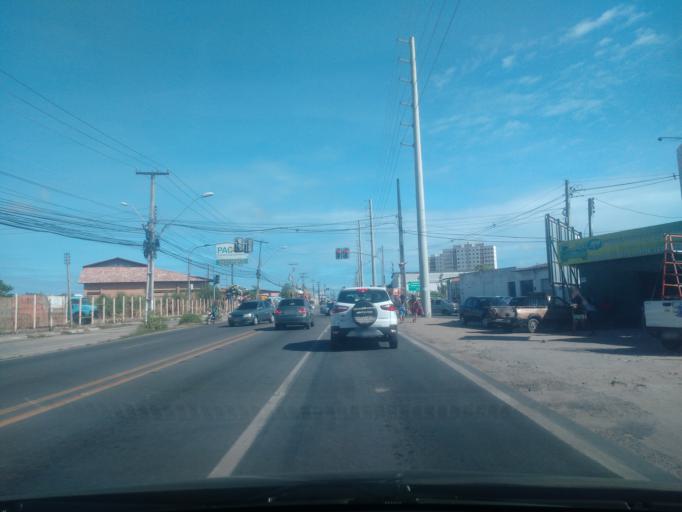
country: BR
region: Alagoas
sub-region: Satuba
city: Satuba
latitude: -9.5641
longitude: -35.7451
